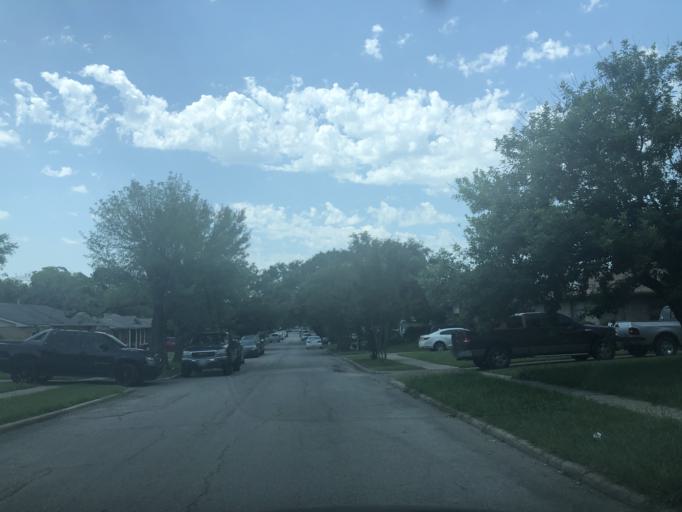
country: US
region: Texas
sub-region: Dallas County
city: Grand Prairie
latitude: 32.7223
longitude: -97.0110
